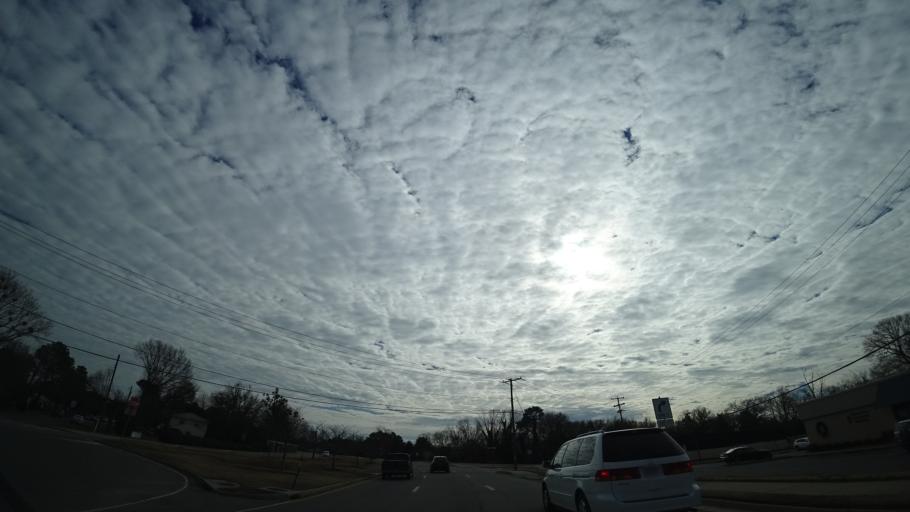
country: US
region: Virginia
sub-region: City of Hampton
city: Hampton
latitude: 37.0422
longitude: -76.3765
